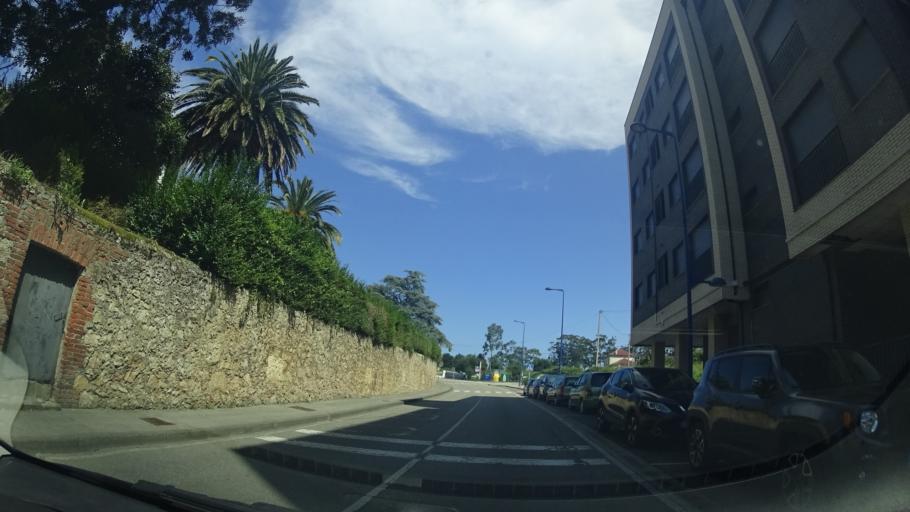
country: ES
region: Asturias
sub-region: Province of Asturias
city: Ribadesella
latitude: 43.4597
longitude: -5.0568
